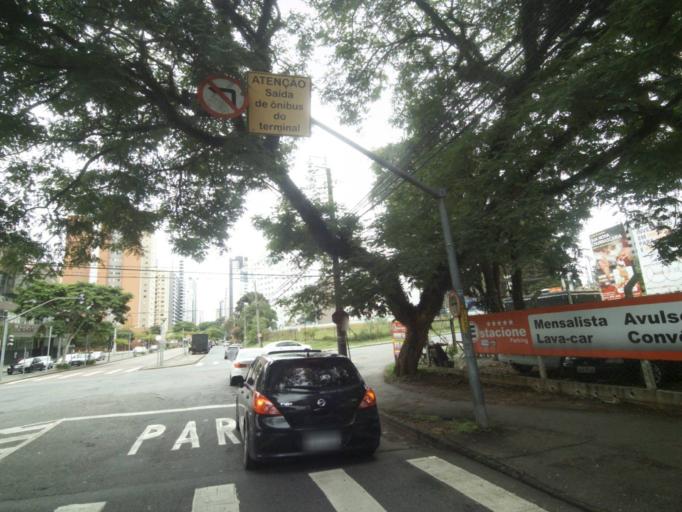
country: BR
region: Parana
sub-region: Curitiba
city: Curitiba
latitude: -25.4359
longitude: -49.3064
